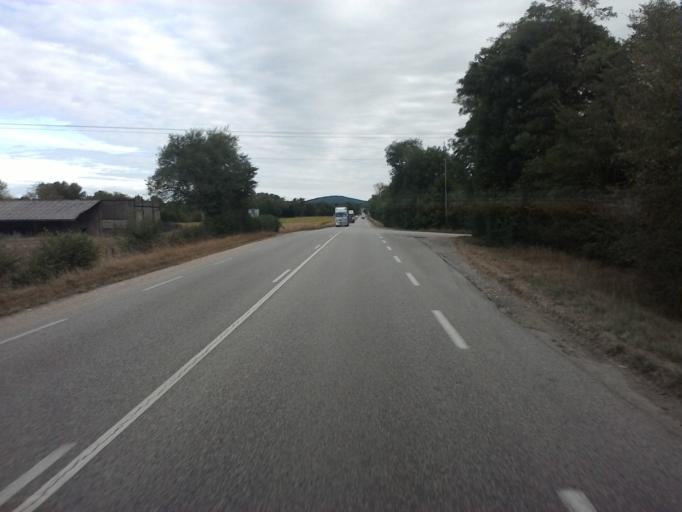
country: FR
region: Rhone-Alpes
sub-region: Departement de l'Ain
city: Ambronay
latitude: 46.0332
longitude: 5.3378
